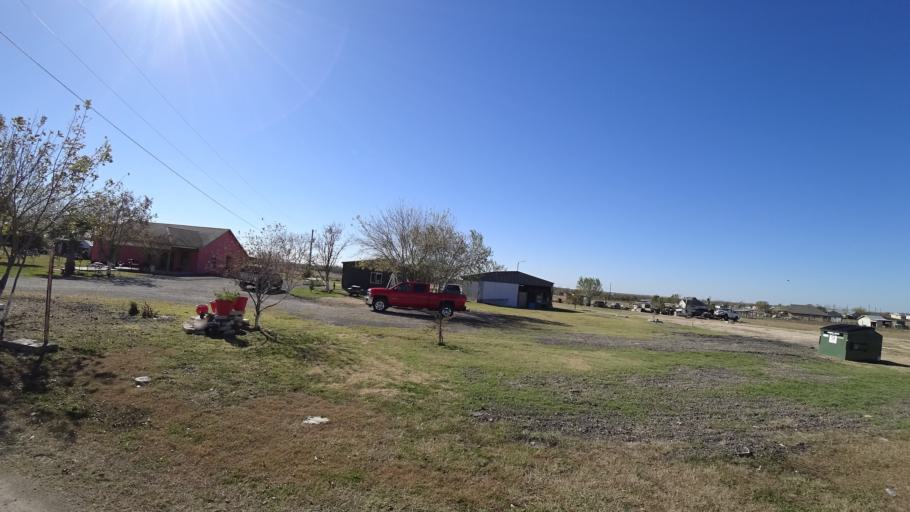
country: US
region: Texas
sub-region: Travis County
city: Garfield
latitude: 30.1000
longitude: -97.6174
